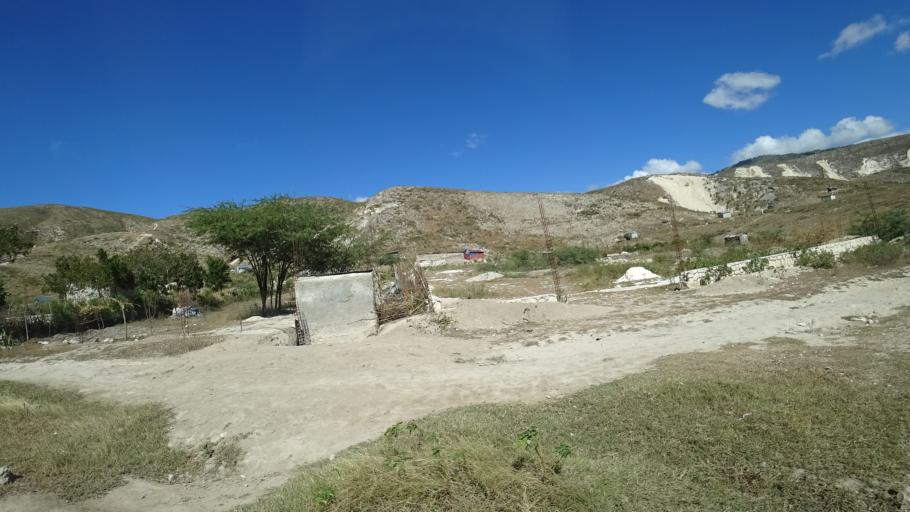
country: HT
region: Ouest
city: Croix des Bouquets
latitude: 18.6754
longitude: -72.2612
